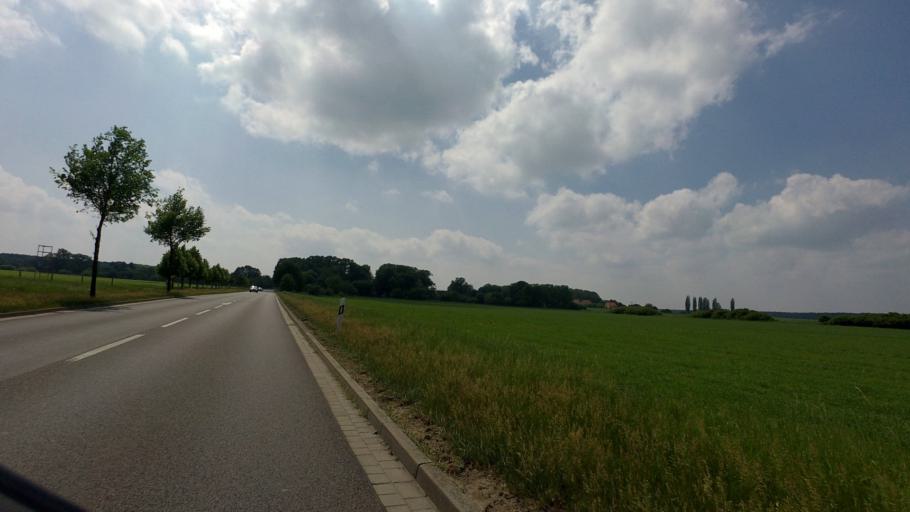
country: DE
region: Brandenburg
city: Cottbus
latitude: 51.6835
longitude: 14.3586
